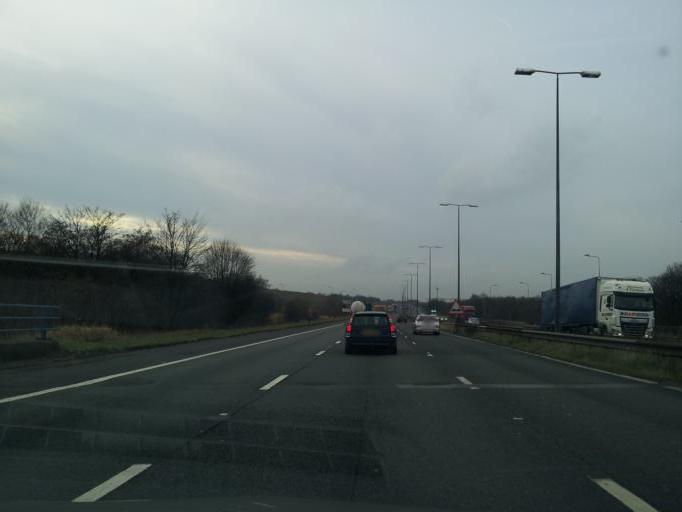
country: GB
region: England
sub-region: Borough of Rochdale
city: Milnrow
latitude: 53.6033
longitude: -2.1068
